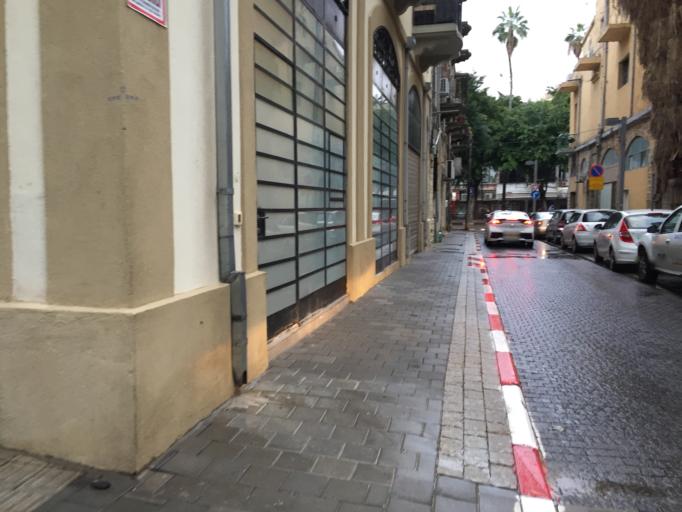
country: IL
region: Tel Aviv
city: Yafo
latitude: 32.0526
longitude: 34.7586
